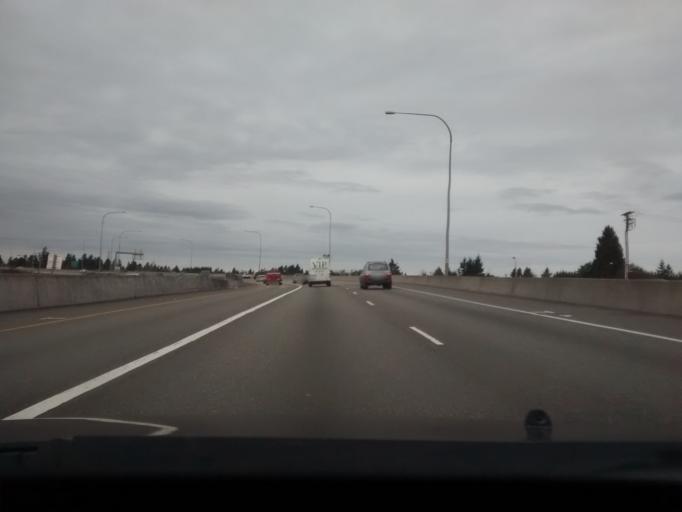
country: US
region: Washington
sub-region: Pierce County
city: Fircrest
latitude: 47.2545
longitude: -122.5136
